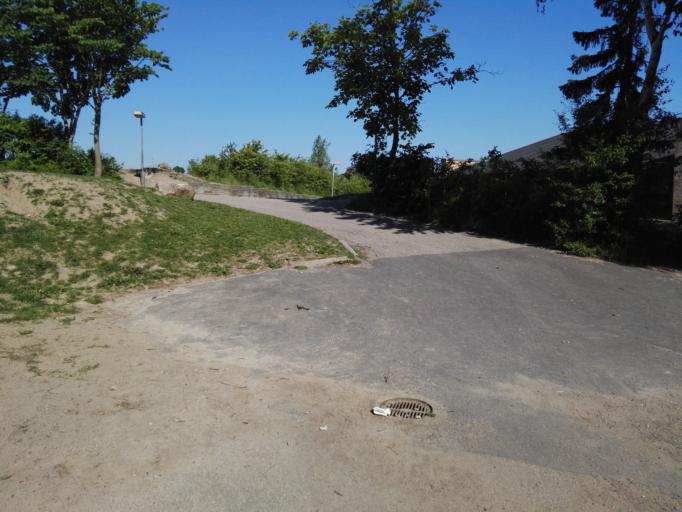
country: DK
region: Zealand
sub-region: Lejre Kommune
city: Ejby
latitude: 55.7079
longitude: 11.8975
